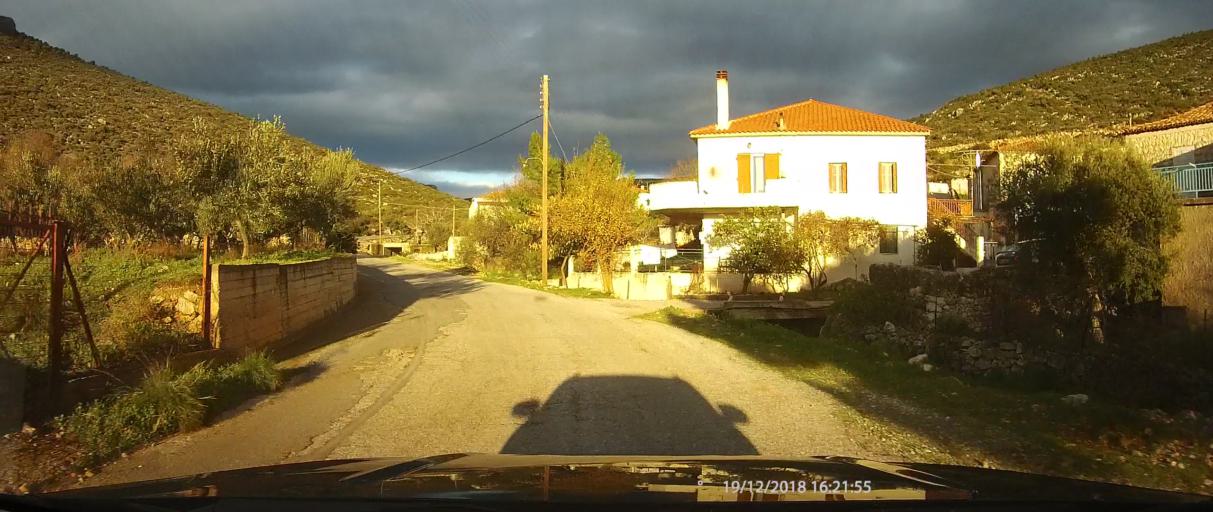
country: GR
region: Peloponnese
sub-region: Nomos Lakonias
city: Kato Glikovrisi
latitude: 36.9391
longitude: 22.8246
